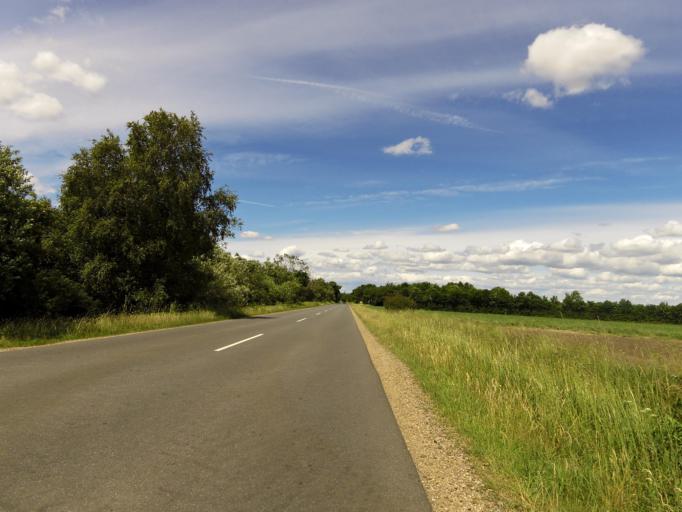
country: DK
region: South Denmark
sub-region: Esbjerg Kommune
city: Ribe
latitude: 55.2833
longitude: 8.7872
